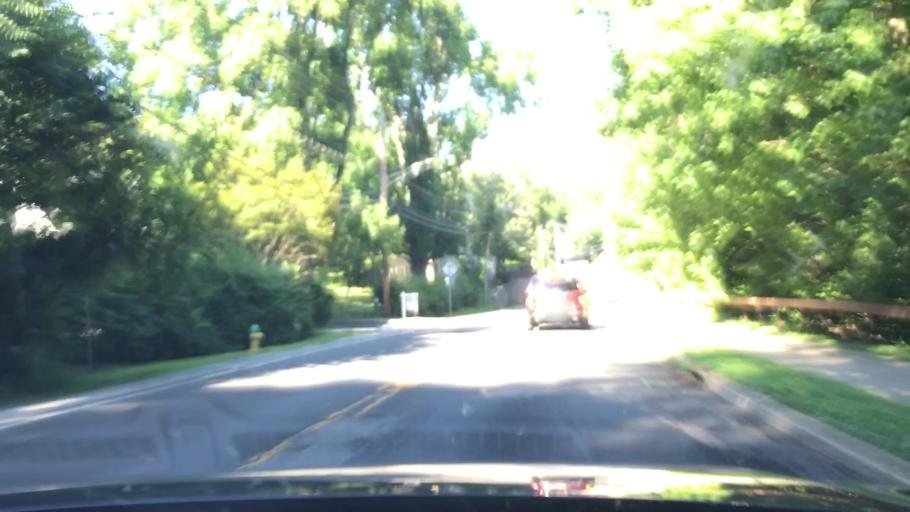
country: US
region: New York
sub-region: Westchester County
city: Pleasantville
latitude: 41.1285
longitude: -73.8010
